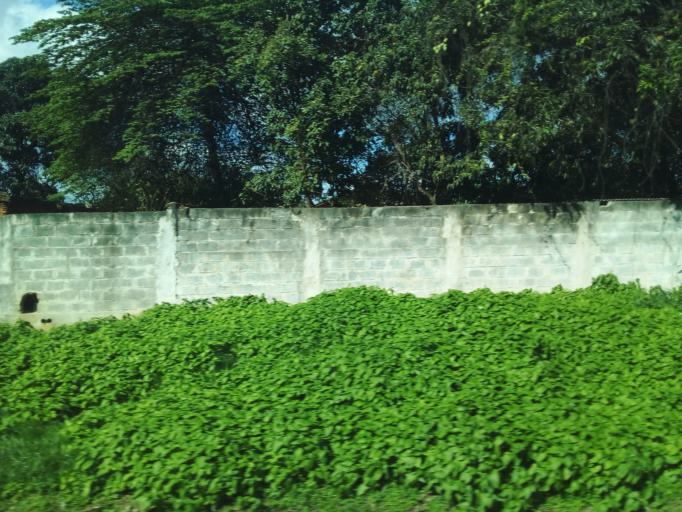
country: BR
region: Minas Gerais
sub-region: Divino Das Laranjeiras
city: Divino das Laranjeiras
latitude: -18.9780
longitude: -41.6530
